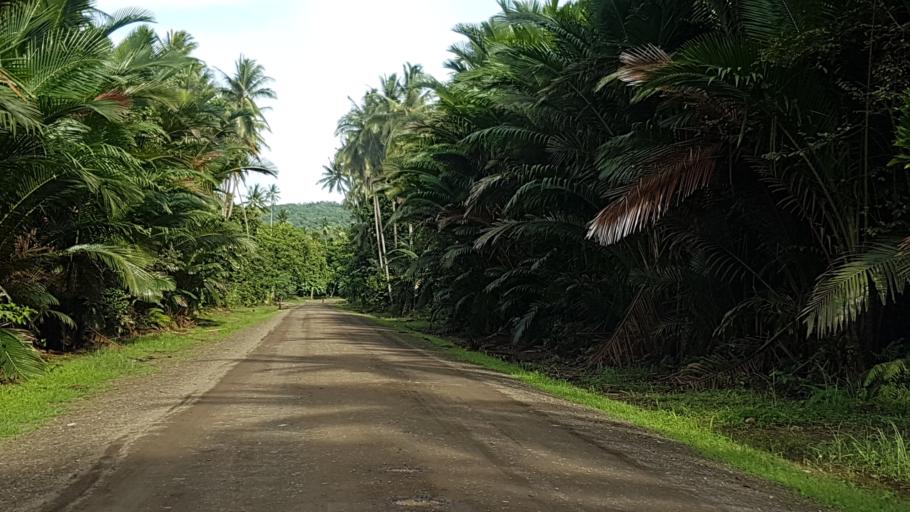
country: PG
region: Milne Bay
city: Alotau
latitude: -10.3164
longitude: 150.7092
